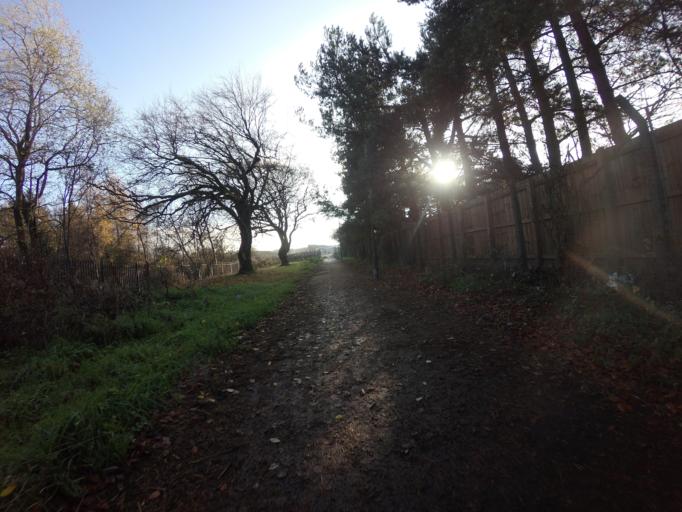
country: GB
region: Scotland
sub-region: West Lothian
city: Livingston
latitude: 55.9132
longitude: -3.5270
